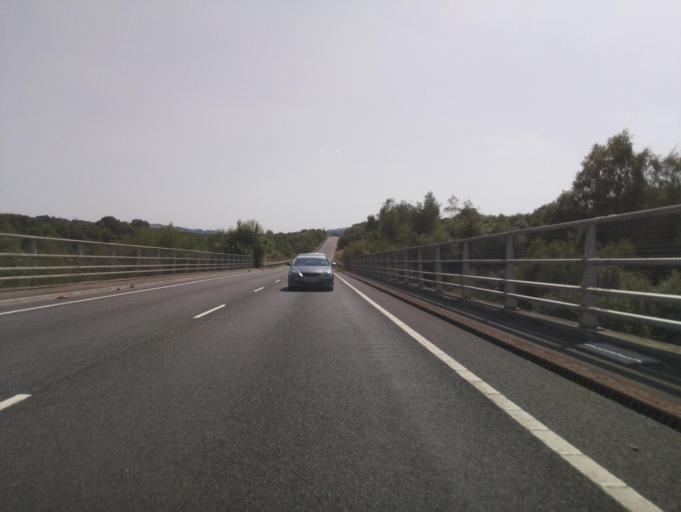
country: GB
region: Wales
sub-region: Caerphilly County Borough
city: Bargoed
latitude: 51.6798
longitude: -3.2227
